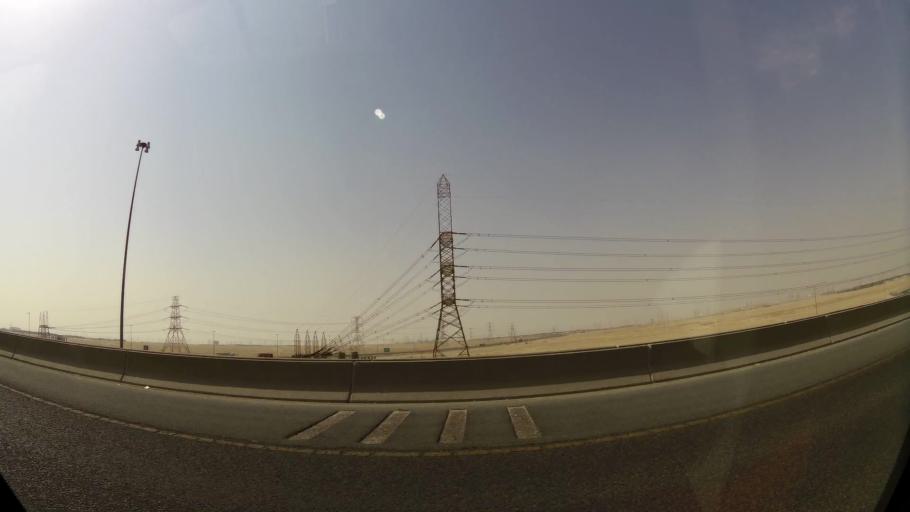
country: KW
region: Al Ahmadi
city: Al Fahahil
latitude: 29.0394
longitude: 48.1171
